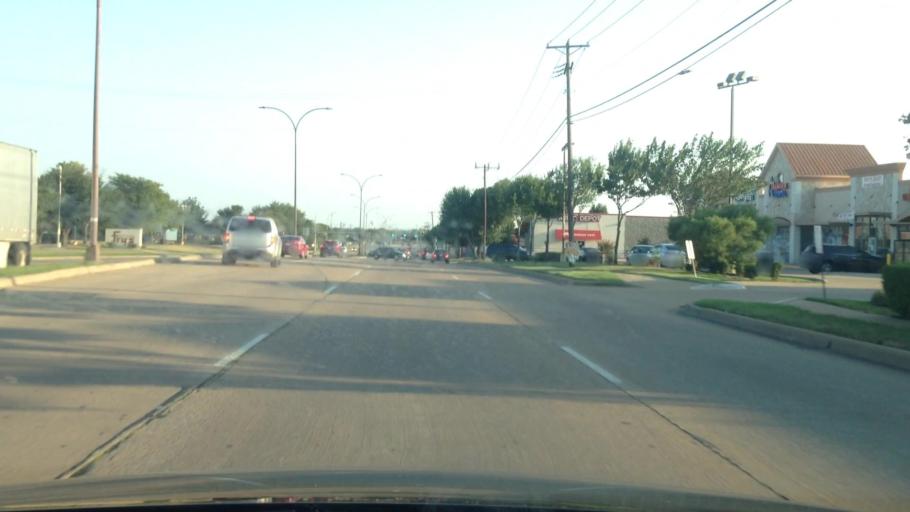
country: US
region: Texas
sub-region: Tarrant County
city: Dalworthington Gardens
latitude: 32.6767
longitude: -97.1151
